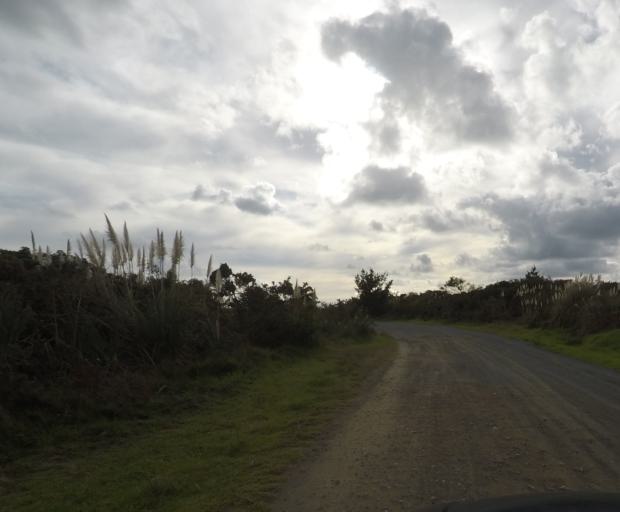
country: NZ
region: Northland
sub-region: Whangarei
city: Ruakaka
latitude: -35.9327
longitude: 174.4588
